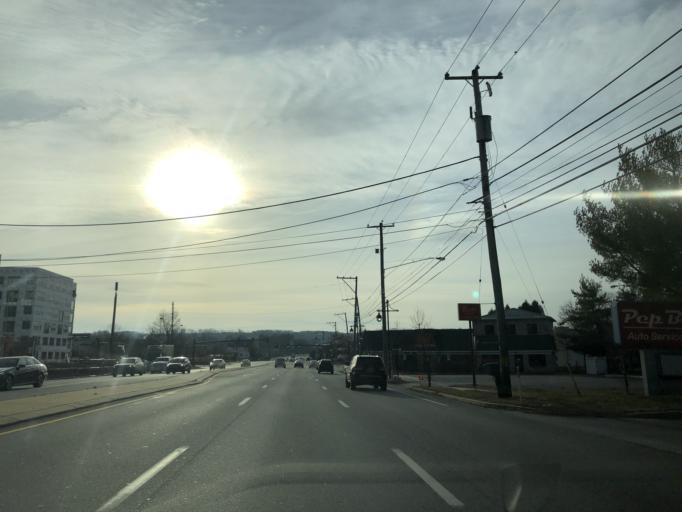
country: US
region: Pennsylvania
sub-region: Chester County
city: Exton
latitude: 40.0321
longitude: -75.6311
